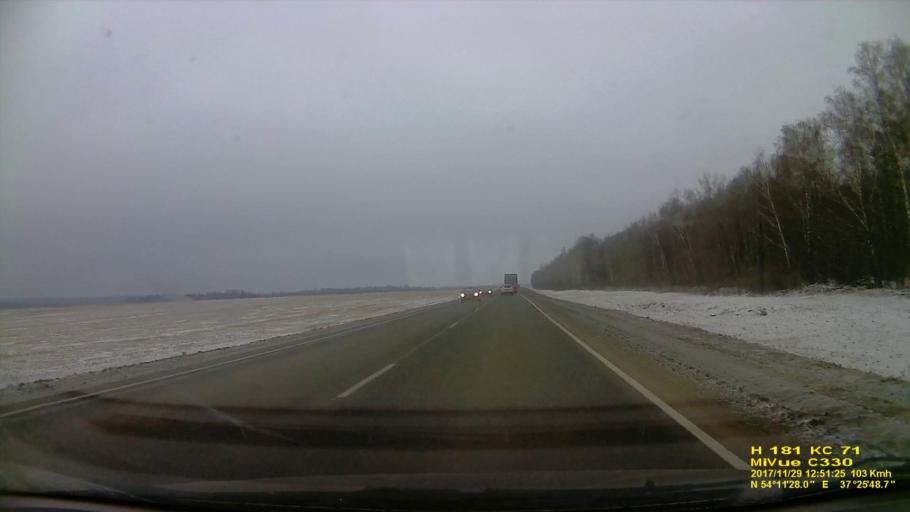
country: RU
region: Tula
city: Barsuki
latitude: 54.1912
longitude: 37.4300
